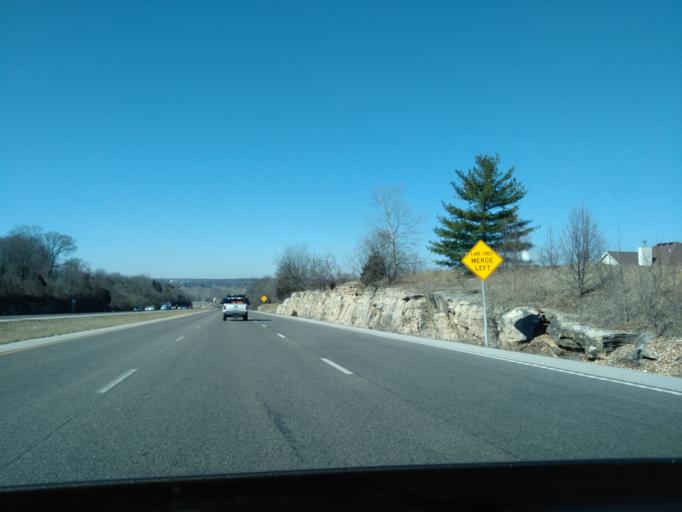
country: US
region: Missouri
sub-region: Saint Louis County
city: Sunset Hills
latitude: 38.5241
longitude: -90.4047
